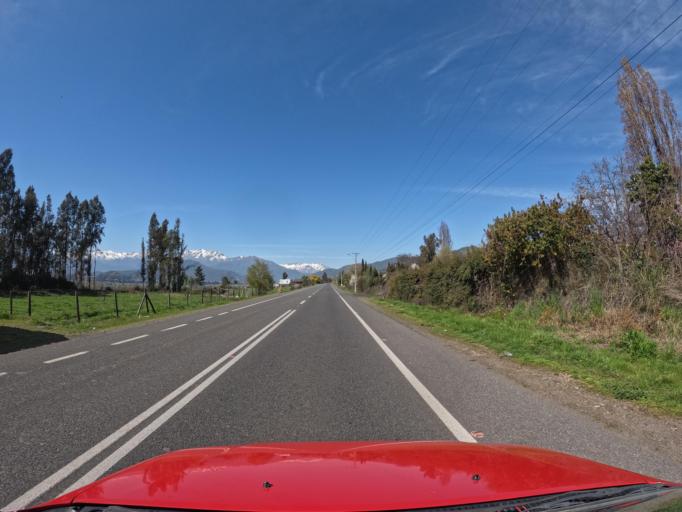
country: CL
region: Maule
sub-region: Provincia de Curico
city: Teno
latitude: -34.9806
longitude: -70.9575
